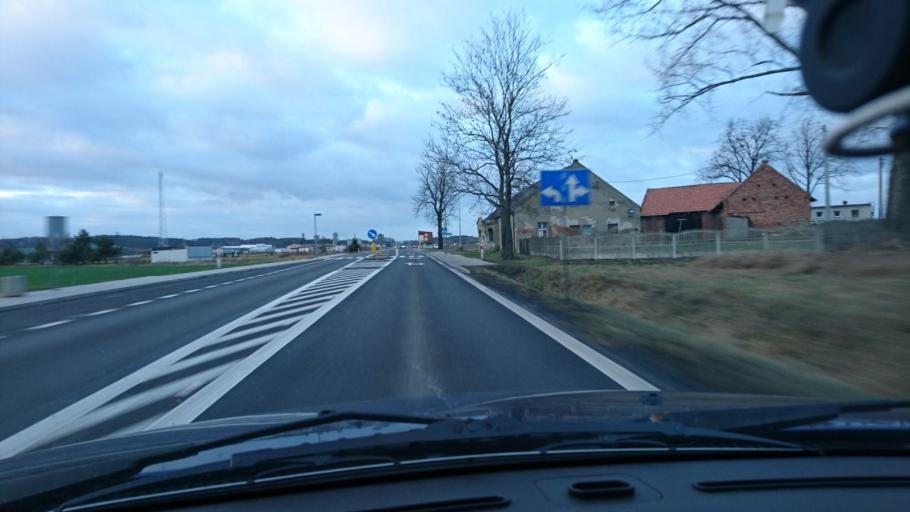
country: PL
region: Greater Poland Voivodeship
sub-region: Powiat ostrzeszowski
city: Ostrzeszow
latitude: 51.3864
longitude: 17.9486
